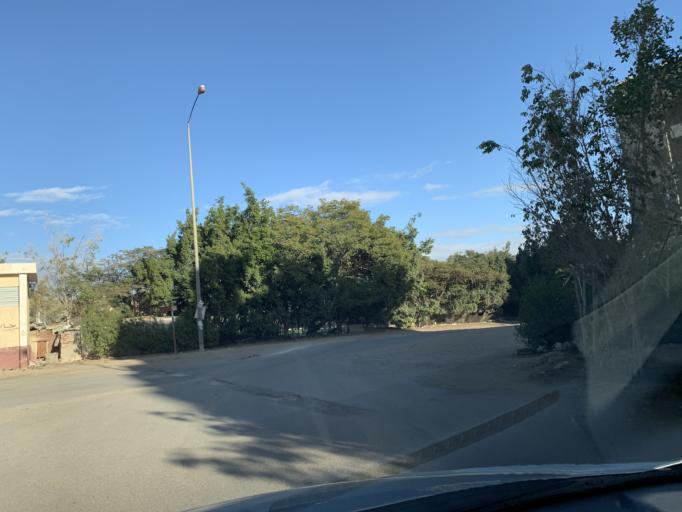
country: EG
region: Al Jizah
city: Madinat Sittah Uktubar
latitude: 29.9747
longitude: 30.9401
